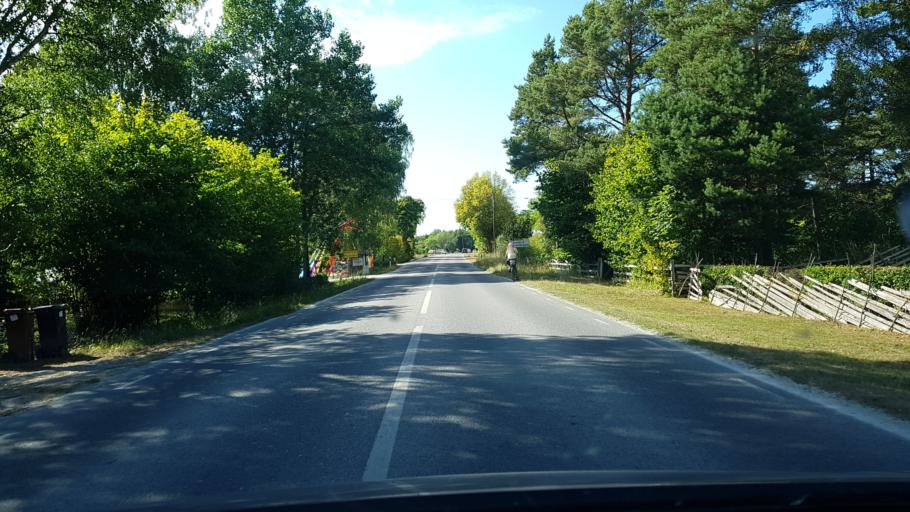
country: SE
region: Gotland
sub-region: Gotland
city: Klintehamn
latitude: 57.4079
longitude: 18.1677
